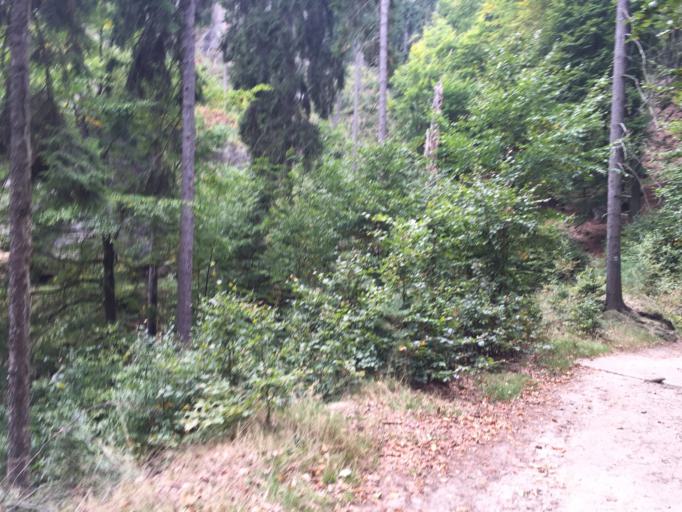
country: CZ
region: Ustecky
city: Ceska Kamenice
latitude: 50.8664
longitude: 14.3913
